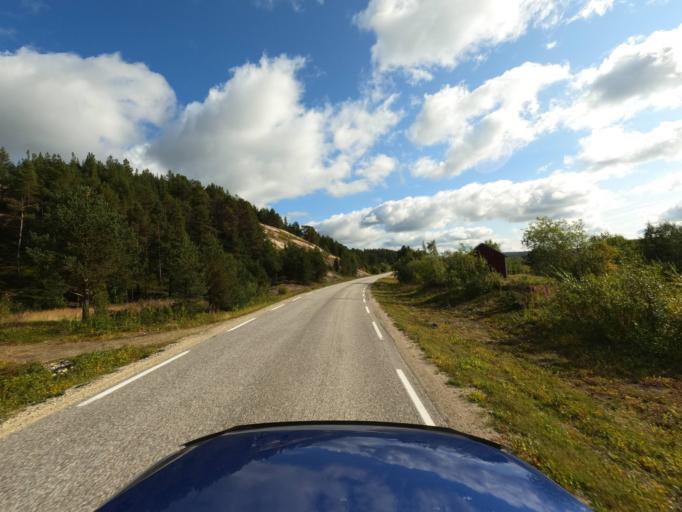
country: NO
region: Finnmark Fylke
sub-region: Karasjok
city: Karasjohka
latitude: 69.4449
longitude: 25.2053
